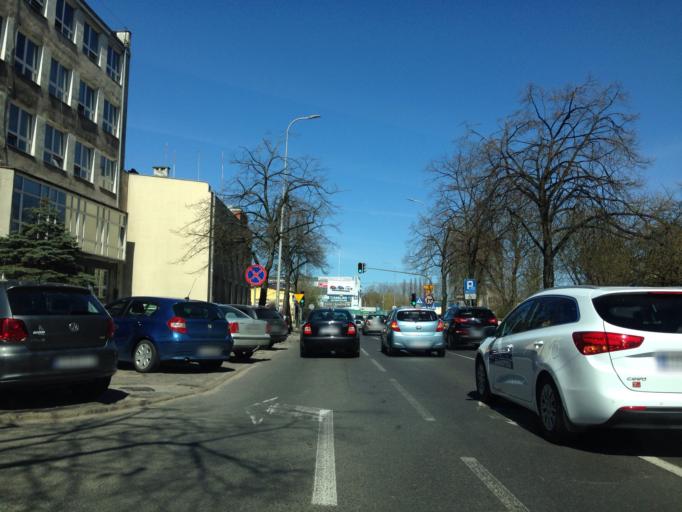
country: PL
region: Pomeranian Voivodeship
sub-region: Gdynia
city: Gdynia
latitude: 54.5226
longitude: 18.5387
